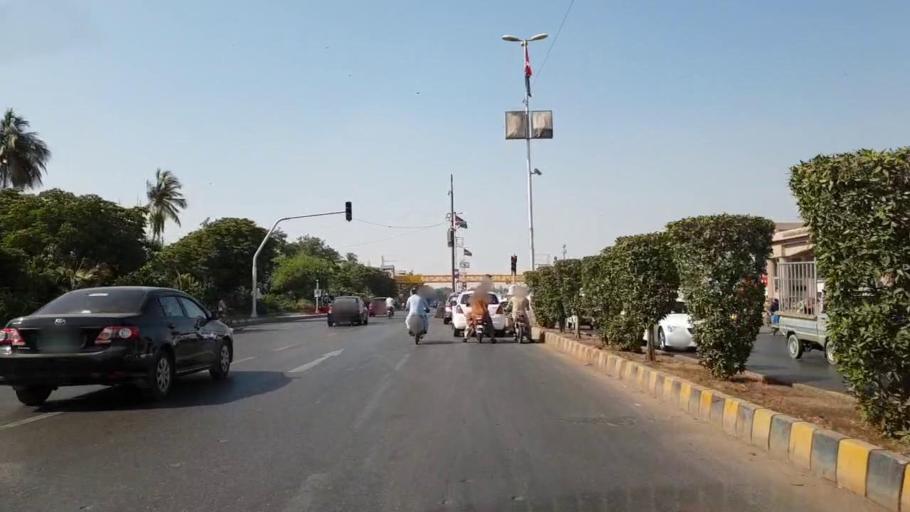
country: PK
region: Sindh
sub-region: Karachi District
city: Karachi
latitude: 24.8794
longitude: 67.0933
